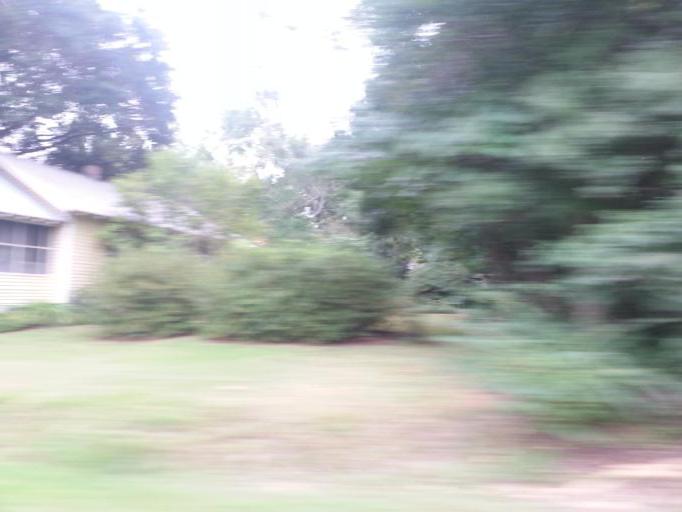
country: US
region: Alabama
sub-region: Baldwin County
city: Fairhope
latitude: 30.5109
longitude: -87.9189
